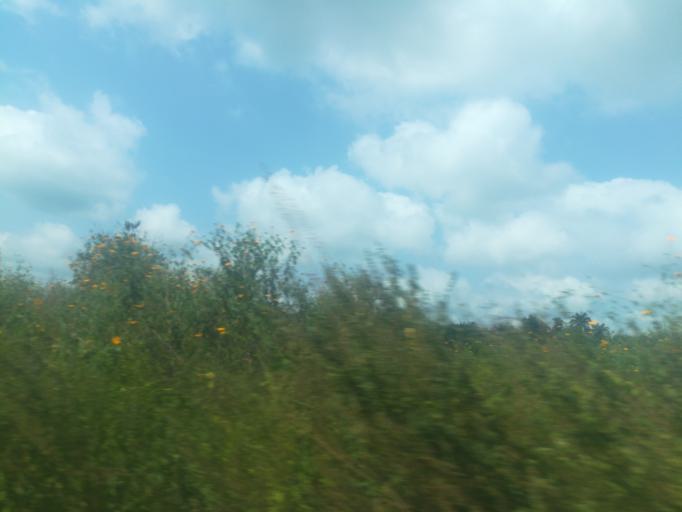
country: NG
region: Oyo
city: Moniya
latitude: 7.5797
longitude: 3.9110
